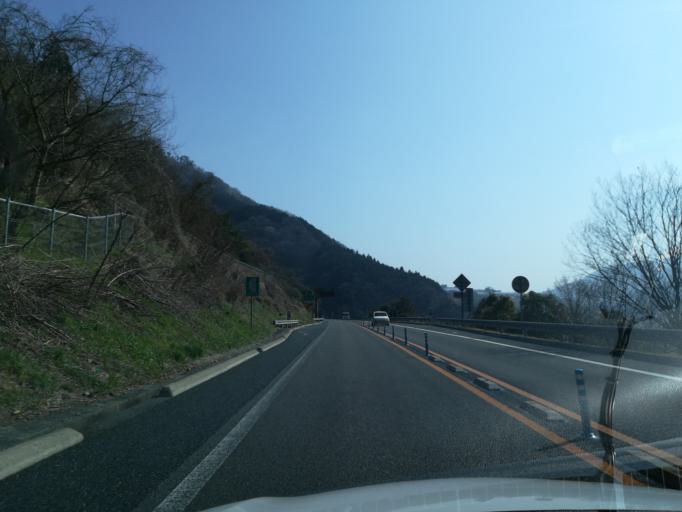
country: JP
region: Tokushima
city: Ikedacho
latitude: 34.0144
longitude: 133.7494
